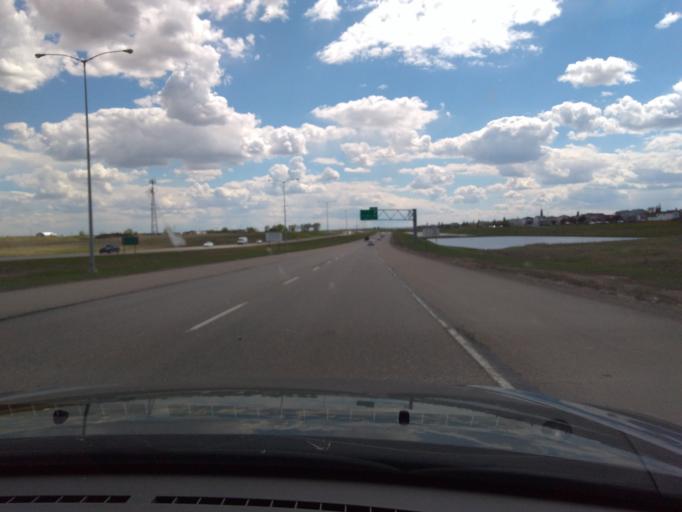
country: CA
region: Alberta
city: Chestermere
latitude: 51.0527
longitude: -113.9208
